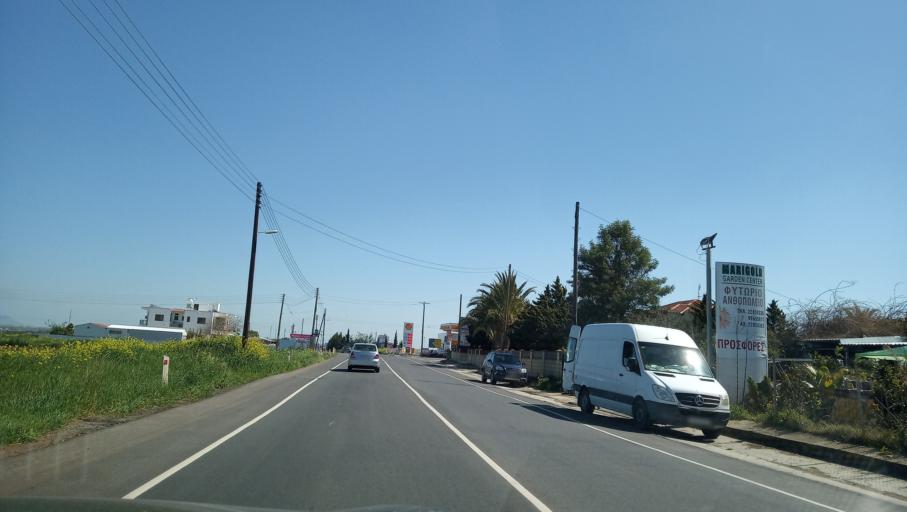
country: CY
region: Lefkosia
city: Peristerona
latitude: 35.1351
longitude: 33.1013
